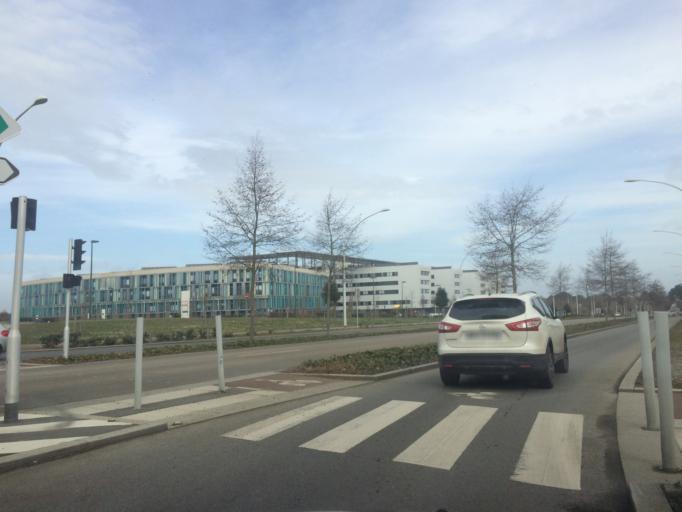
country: FR
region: Pays de la Loire
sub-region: Departement de la Loire-Atlantique
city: Saint-Nazaire
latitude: 47.2645
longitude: -2.2577
